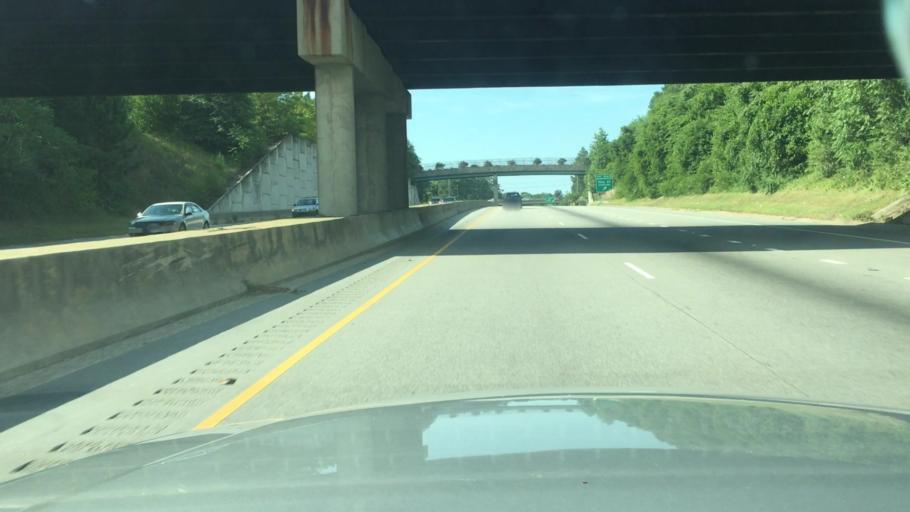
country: US
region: North Carolina
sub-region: Cumberland County
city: Fayetteville
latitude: 35.0524
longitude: -78.8939
